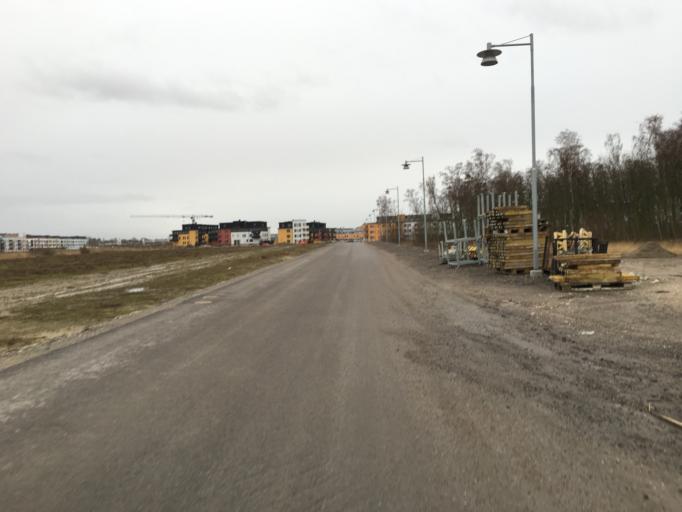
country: SE
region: Skane
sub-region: Lomma Kommun
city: Lomma
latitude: 55.6813
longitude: 13.0626
